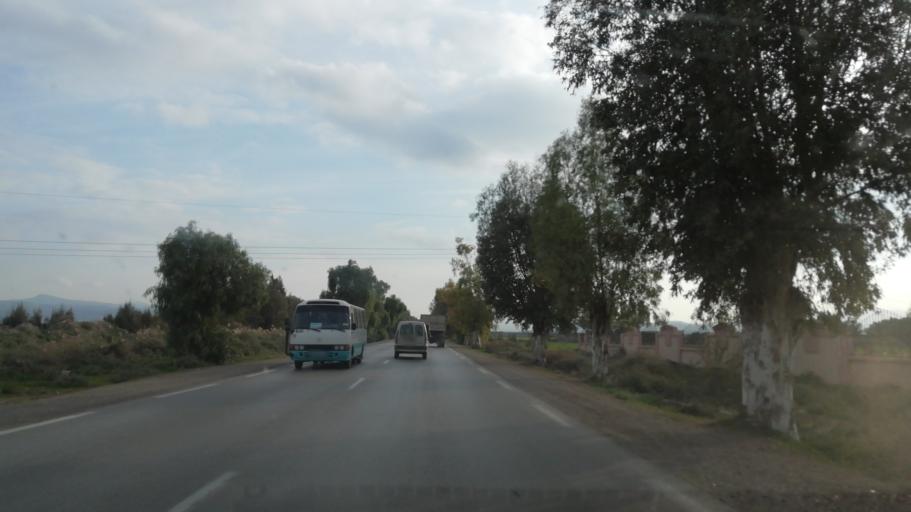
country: DZ
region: Mascara
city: Mascara
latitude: 35.6378
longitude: 0.0606
